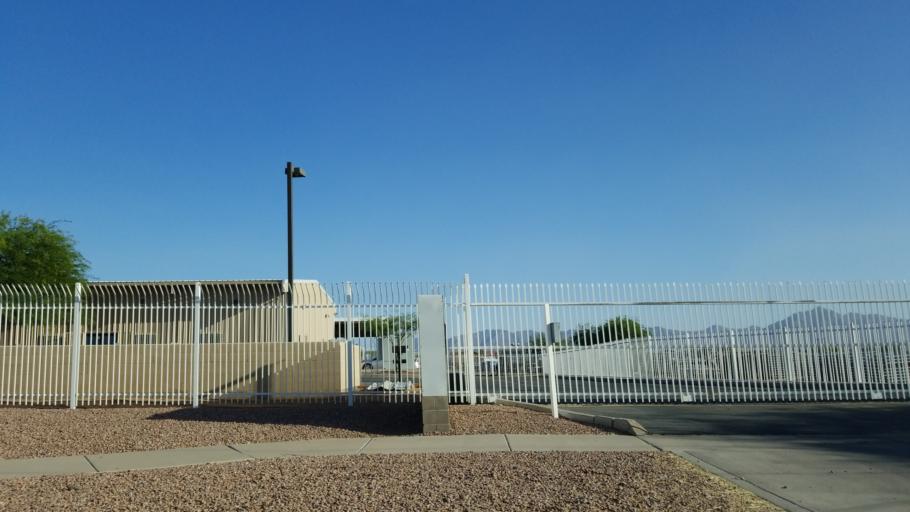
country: US
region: Arizona
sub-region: Maricopa County
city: Laveen
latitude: 33.3918
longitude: -112.2086
